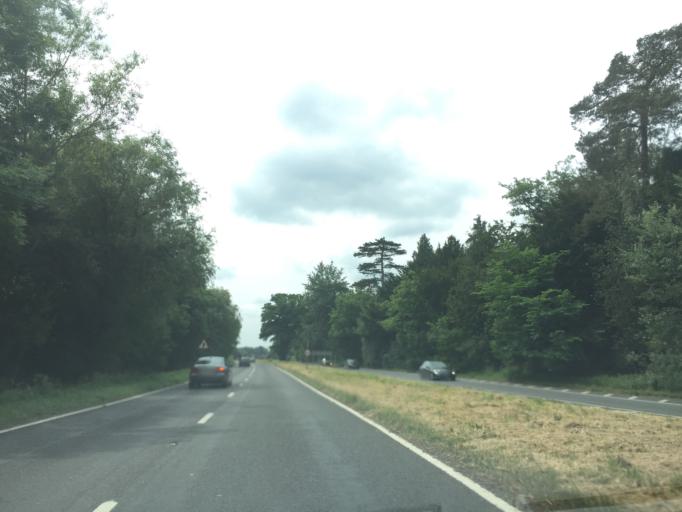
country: GB
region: England
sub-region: Surrey
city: Farnham
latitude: 51.1948
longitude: -0.8441
